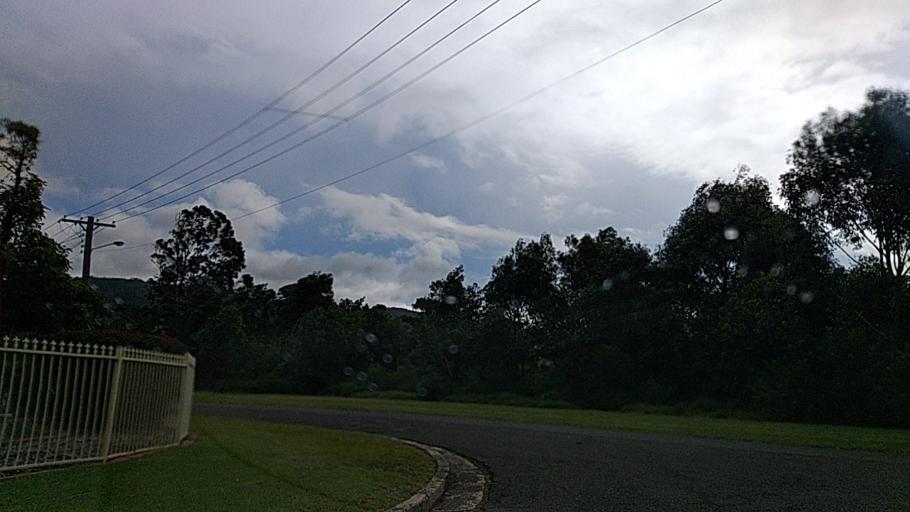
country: AU
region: New South Wales
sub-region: Wollongong
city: Bulli
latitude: -34.3454
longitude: 150.9146
